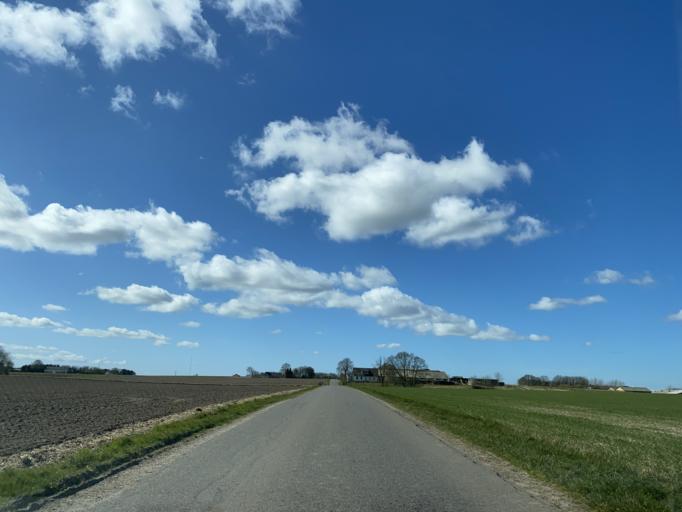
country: DK
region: Central Jutland
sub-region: Favrskov Kommune
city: Ulstrup
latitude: 56.3433
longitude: 9.8283
